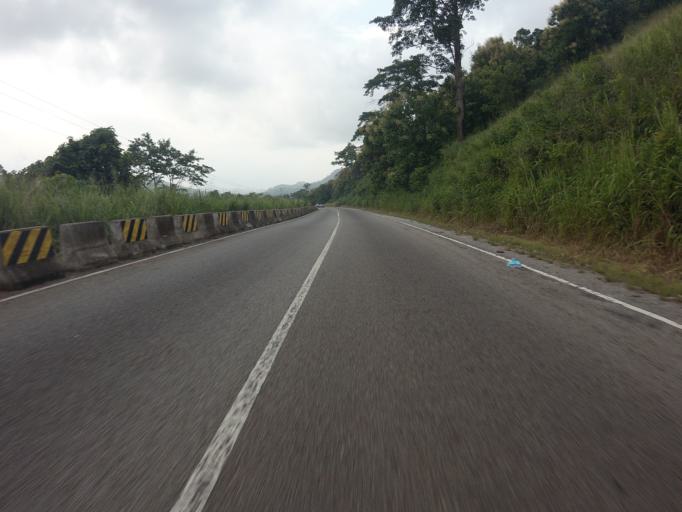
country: GH
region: Volta
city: Ho
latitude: 6.6363
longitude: 0.4663
